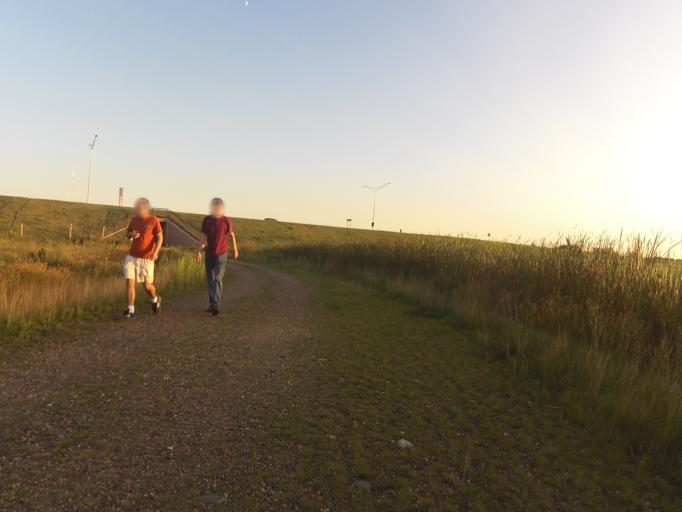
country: US
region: Minnesota
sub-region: Washington County
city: Stillwater
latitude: 45.0601
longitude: -92.7837
